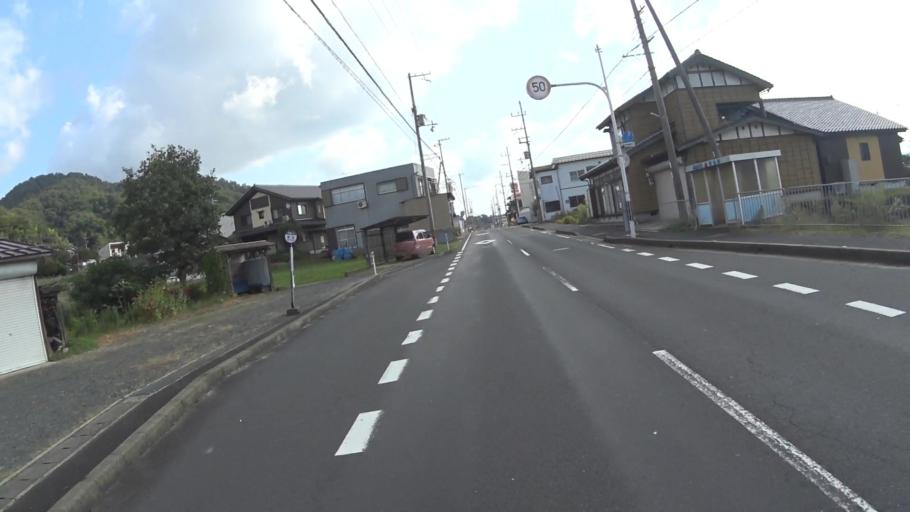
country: JP
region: Kyoto
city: Miyazu
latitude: 35.5788
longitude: 135.1856
